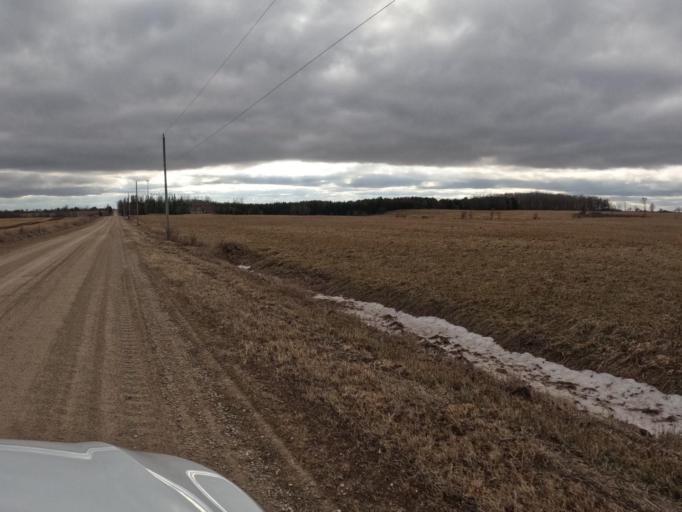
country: CA
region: Ontario
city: Shelburne
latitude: 43.8824
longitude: -80.3814
